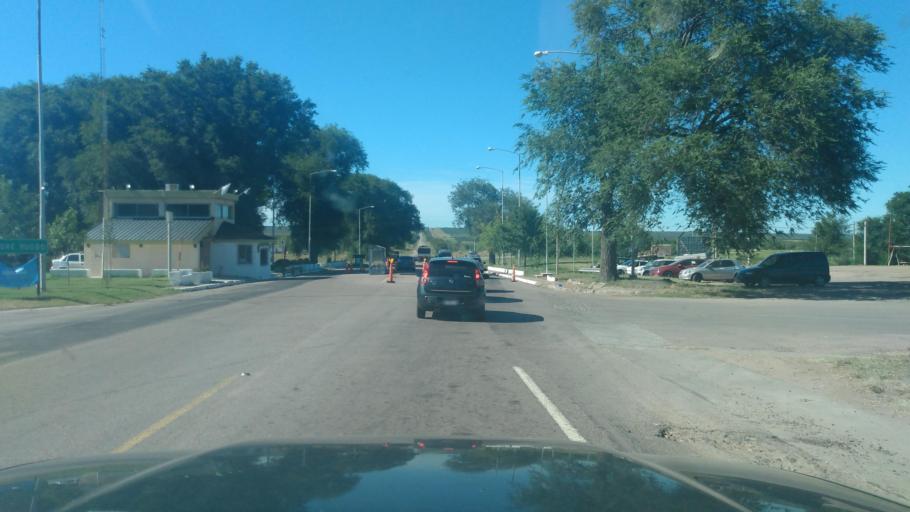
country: AR
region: La Pampa
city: Doblas
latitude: -37.3076
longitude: -64.2880
